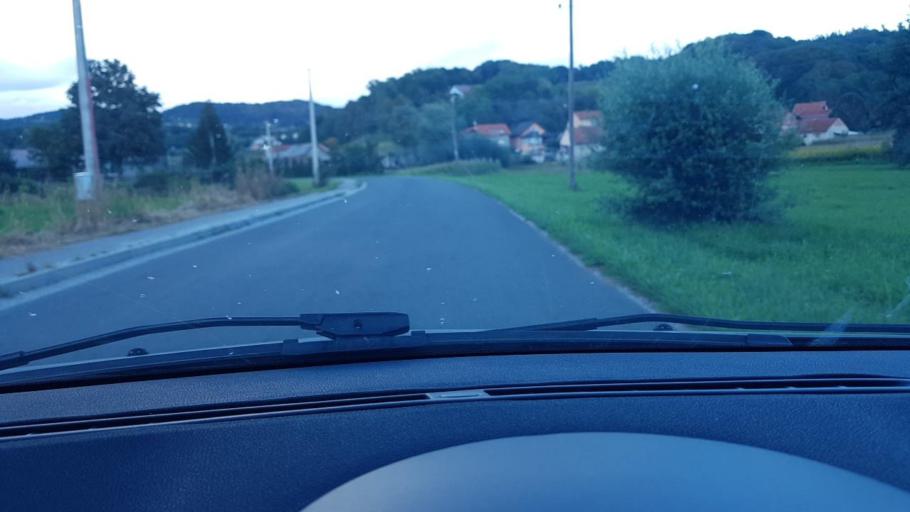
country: HR
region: Krapinsko-Zagorska
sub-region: Grad Krapina
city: Krapina
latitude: 46.1494
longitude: 15.8225
